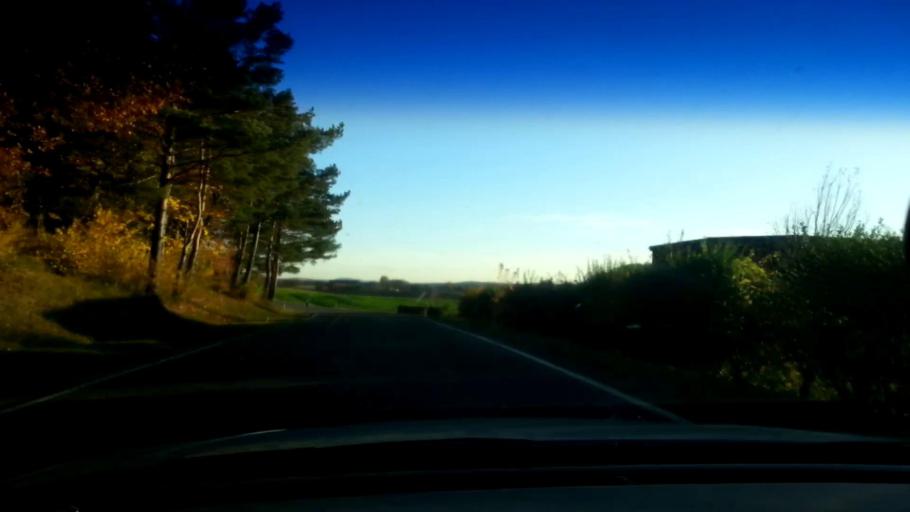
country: DE
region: Bavaria
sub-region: Upper Franconia
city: Heiligenstadt
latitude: 49.8582
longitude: 11.2104
